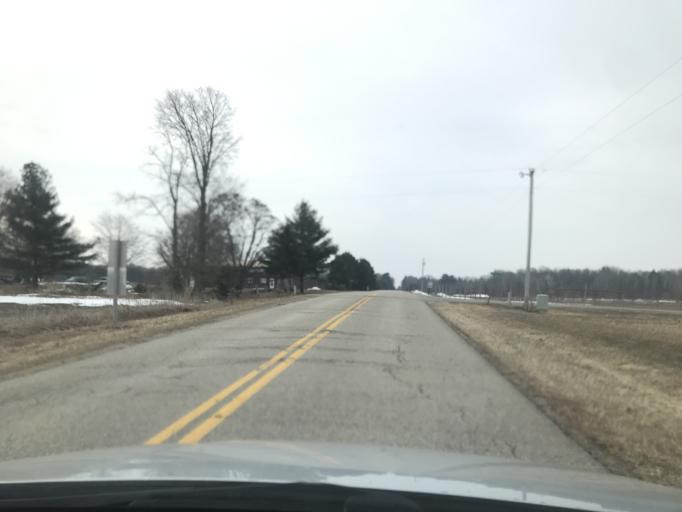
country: US
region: Wisconsin
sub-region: Oconto County
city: Oconto Falls
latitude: 44.8299
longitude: -88.1684
